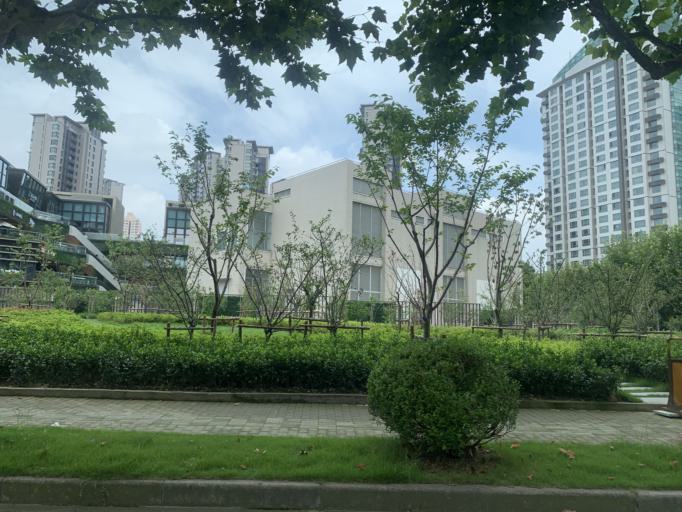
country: CN
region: Shanghai Shi
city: Huamu
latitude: 31.2110
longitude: 121.5329
